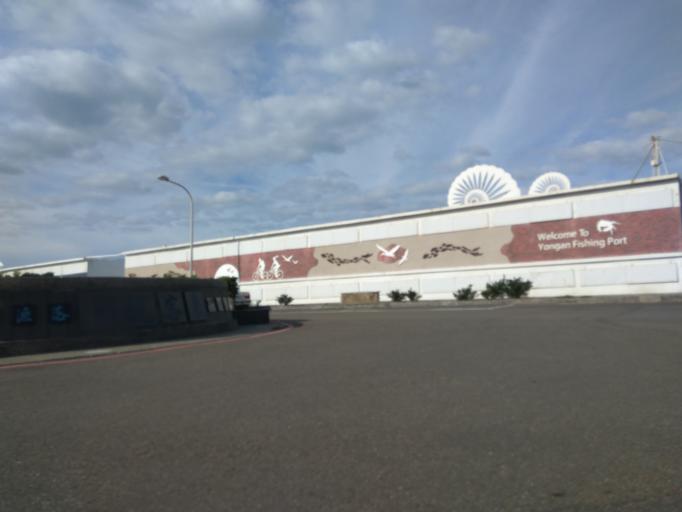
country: TW
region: Taiwan
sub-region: Hsinchu
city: Zhubei
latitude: 24.9873
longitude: 121.0176
